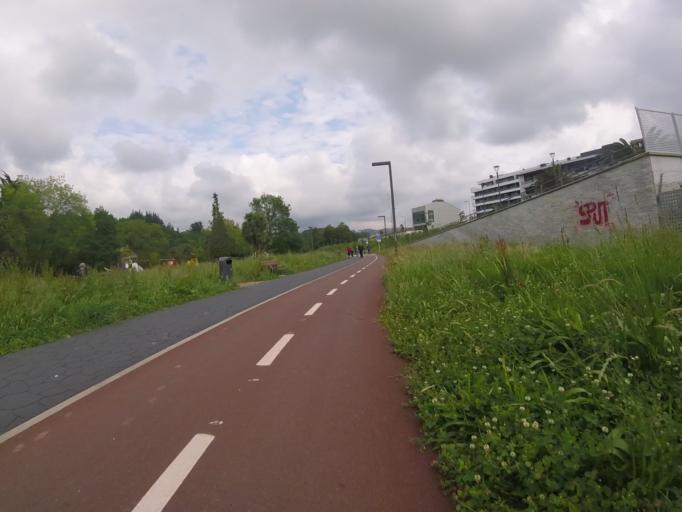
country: ES
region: Basque Country
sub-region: Provincia de Guipuzcoa
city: San Sebastian
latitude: 43.3053
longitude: -1.9583
